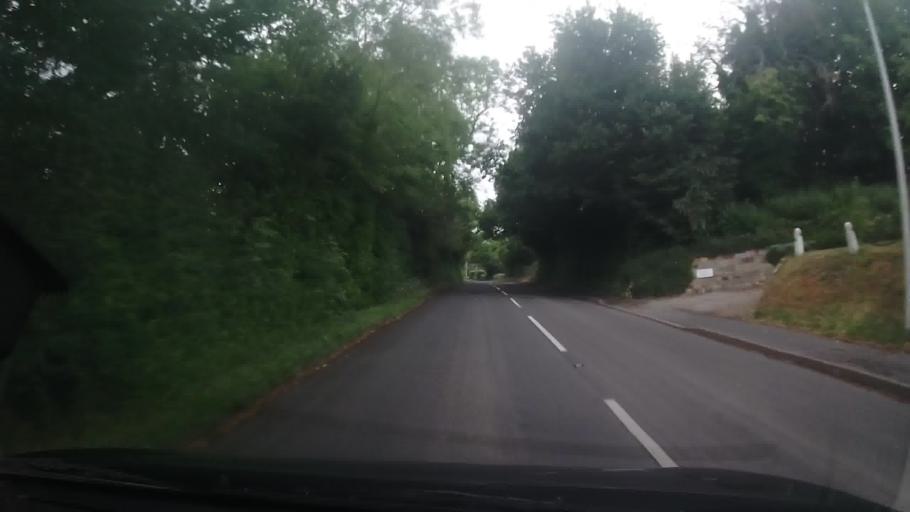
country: GB
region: England
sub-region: Shropshire
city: Shrewsbury
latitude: 52.7202
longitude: -2.7631
